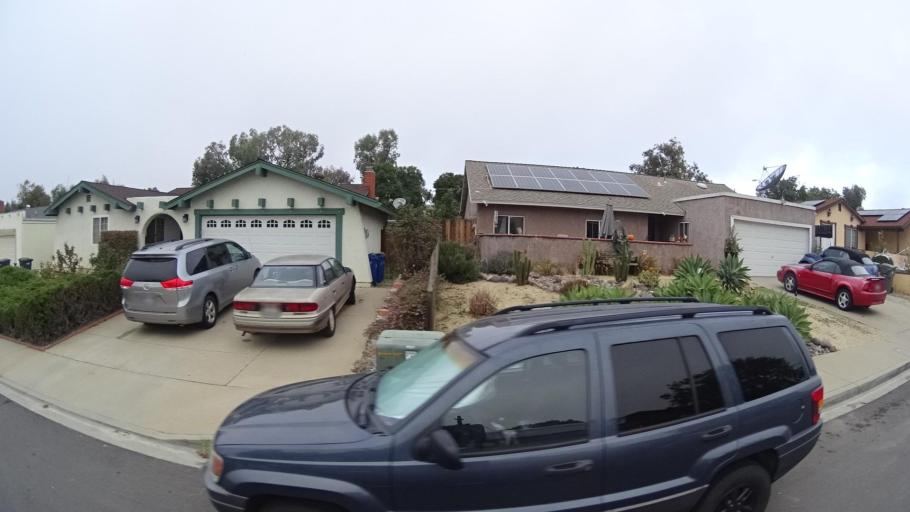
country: US
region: California
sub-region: San Diego County
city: Rancho San Diego
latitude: 32.7317
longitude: -116.9588
